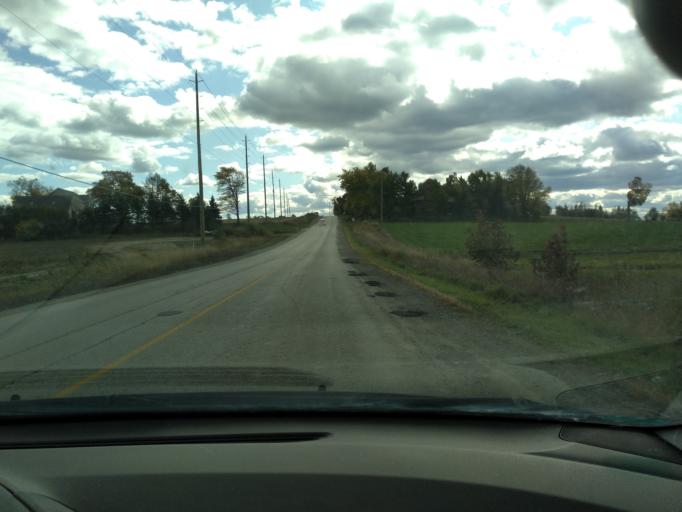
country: CA
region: Ontario
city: Bradford West Gwillimbury
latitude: 44.0892
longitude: -79.5975
